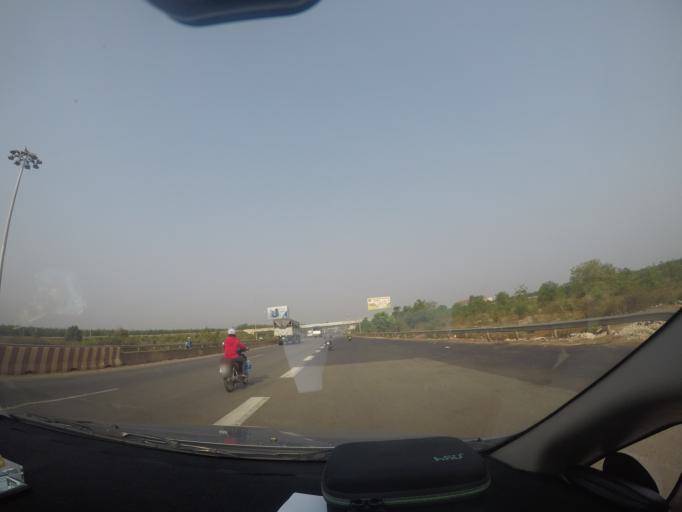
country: VN
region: Dong Nai
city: Thong Nhat
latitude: 10.9424
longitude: 107.1650
